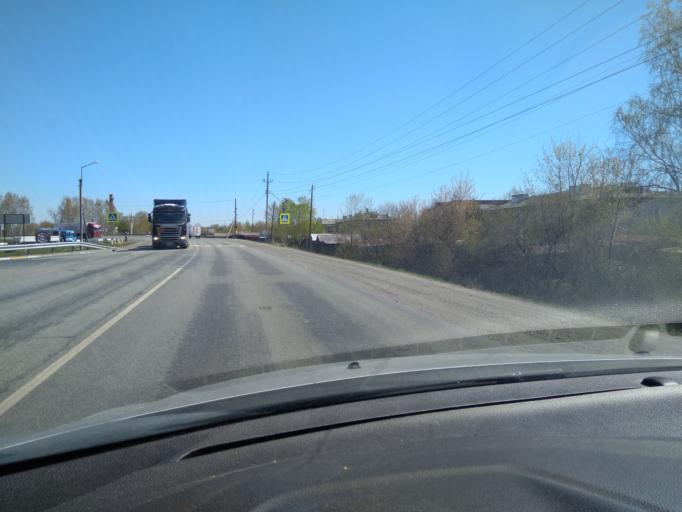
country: RU
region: Sverdlovsk
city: Pyshma
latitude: 56.9521
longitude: 63.2310
